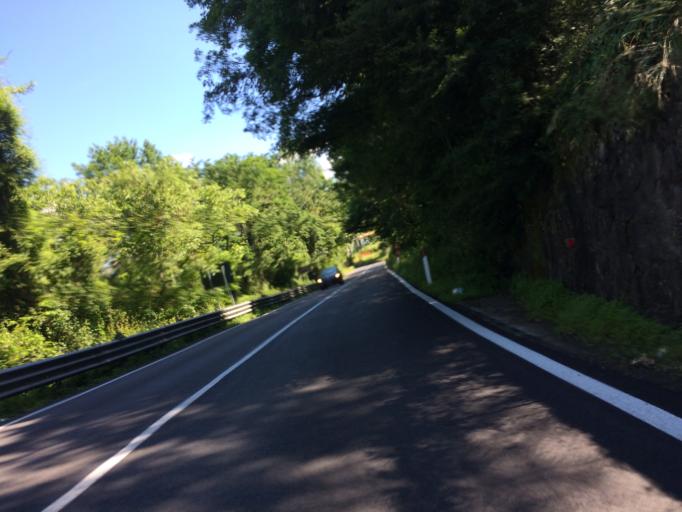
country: IT
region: Tuscany
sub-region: Provincia di Massa-Carrara
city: Terrarossa
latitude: 44.2433
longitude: 9.9593
